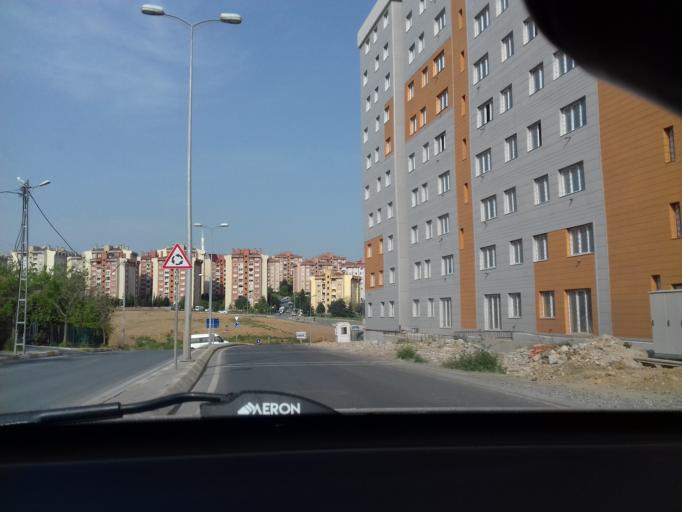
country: TR
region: Istanbul
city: Pendik
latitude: 40.9057
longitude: 29.2726
